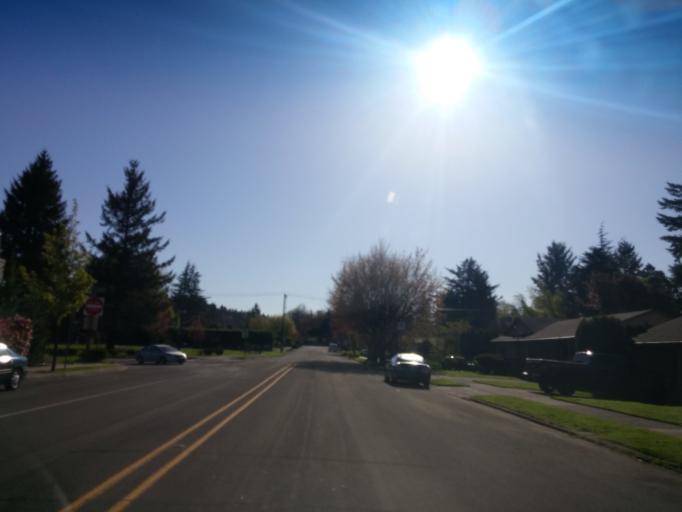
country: US
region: Oregon
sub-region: Washington County
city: West Haven-Sylvan
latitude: 45.5058
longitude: -122.7778
